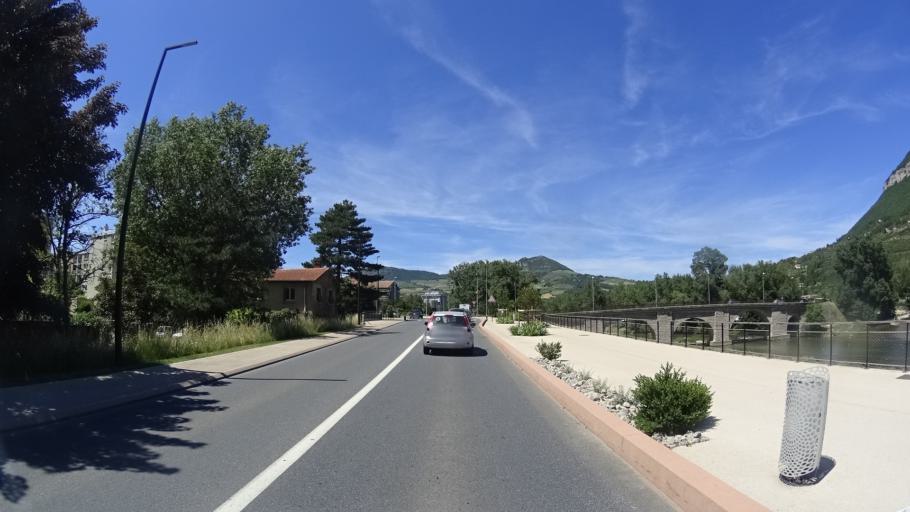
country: FR
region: Midi-Pyrenees
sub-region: Departement de l'Aveyron
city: Millau
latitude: 44.1009
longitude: 3.0864
